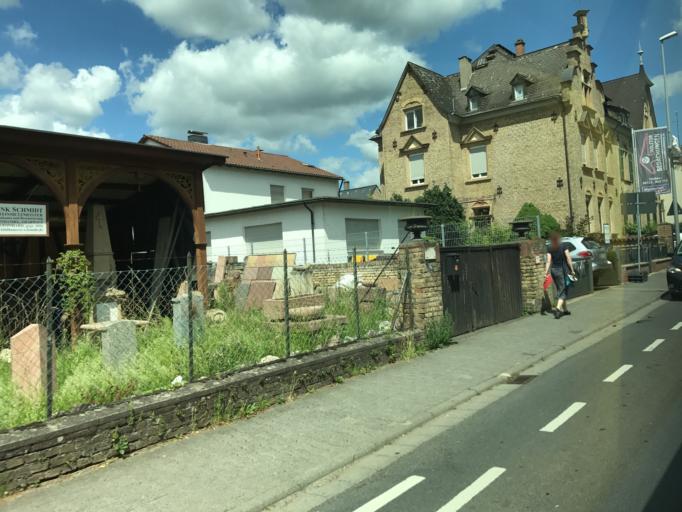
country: DE
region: Hesse
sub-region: Regierungsbezirk Darmstadt
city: Eltville
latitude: 50.0307
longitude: 8.1175
